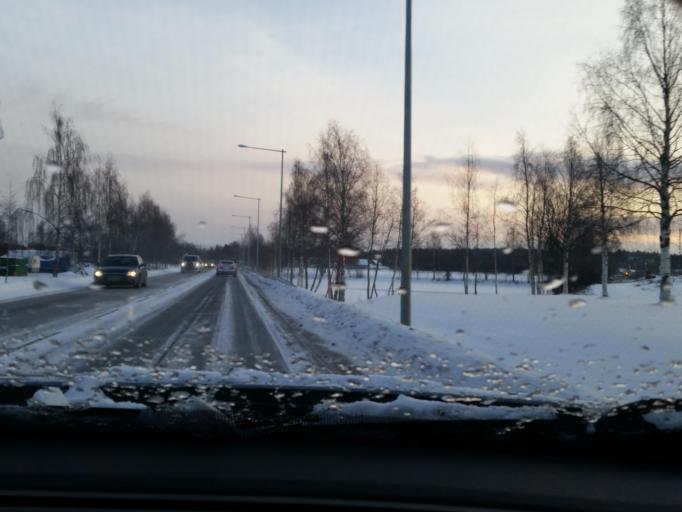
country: SE
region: Norrbotten
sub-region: Pitea Kommun
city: Pitea
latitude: 65.3141
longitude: 21.4797
